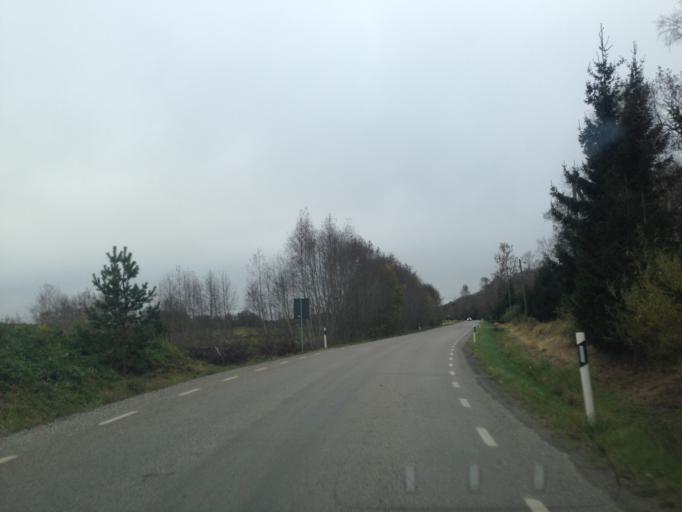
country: EE
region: Harju
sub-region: Saue linn
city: Saue
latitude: 59.3720
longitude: 24.5443
